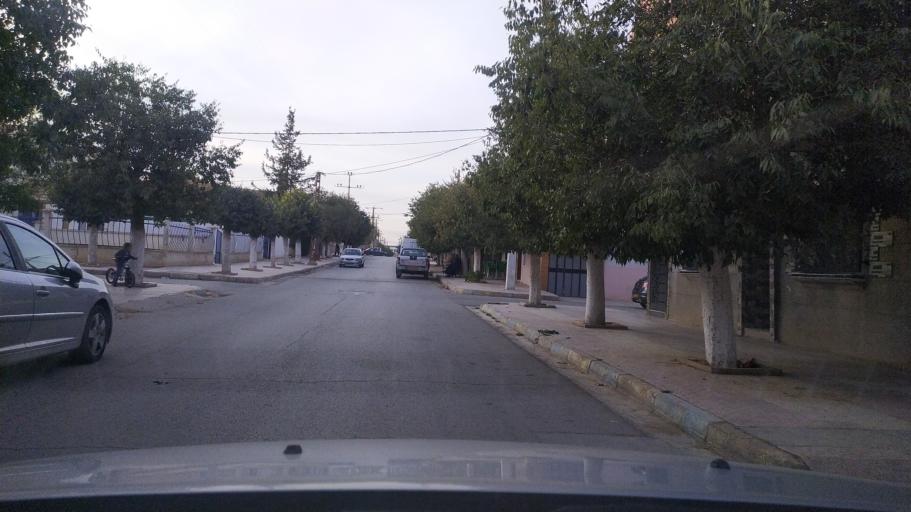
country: DZ
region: Tiaret
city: Frenda
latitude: 34.8987
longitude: 1.2390
